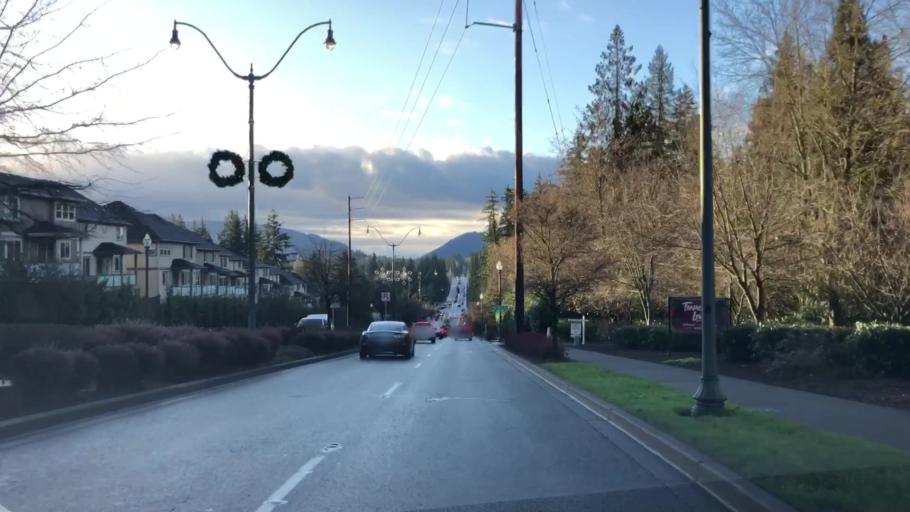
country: US
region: Washington
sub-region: King County
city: City of Sammamish
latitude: 47.5941
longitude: -122.0356
